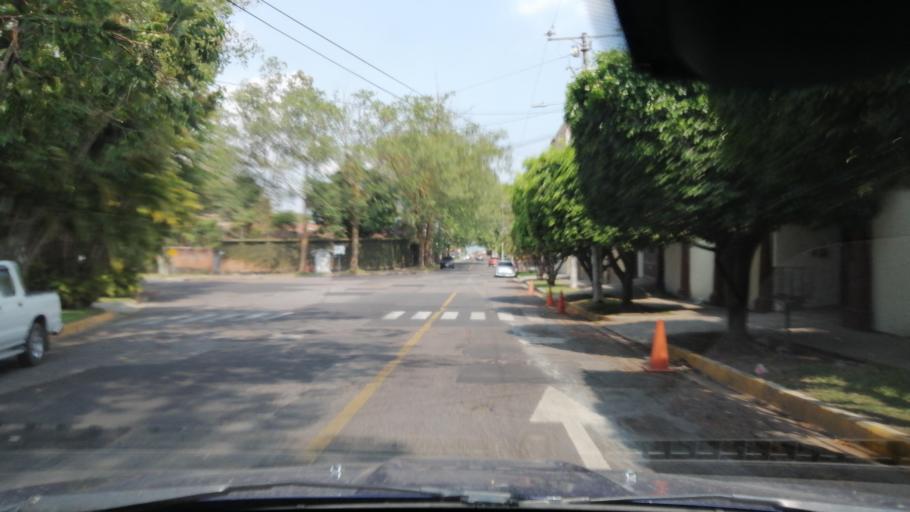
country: SV
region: La Libertad
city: Antiguo Cuscatlan
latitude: 13.6982
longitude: -89.2481
